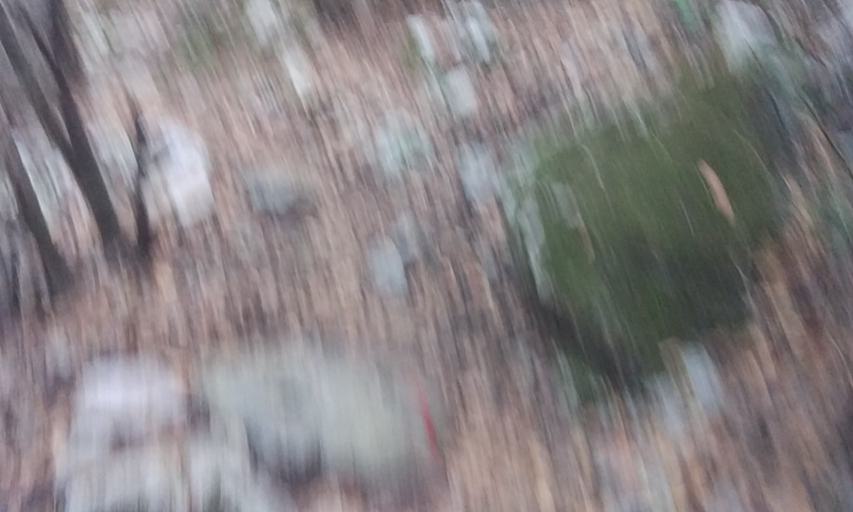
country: TR
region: Antalya
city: Tekirova
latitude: 36.3788
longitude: 30.4772
